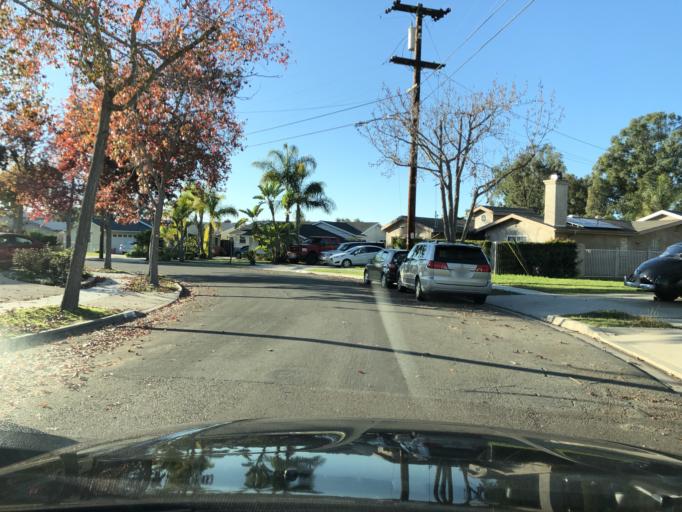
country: US
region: California
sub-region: San Diego County
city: La Jolla
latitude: 32.8217
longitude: -117.1902
